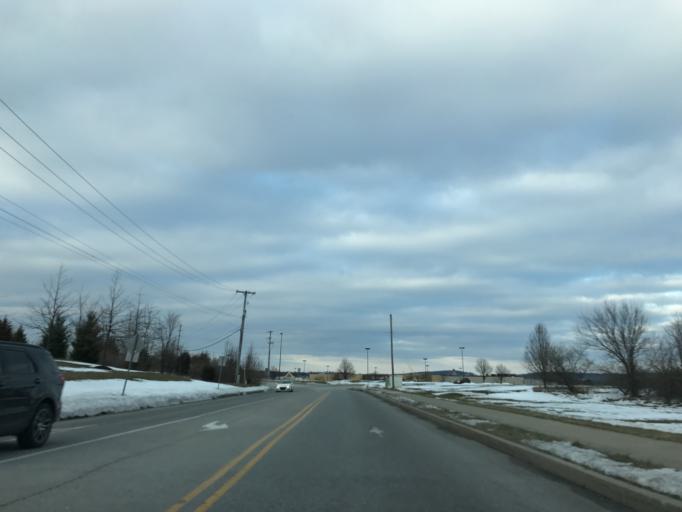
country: US
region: Pennsylvania
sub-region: York County
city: Shrewsbury
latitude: 39.7656
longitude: -76.6722
